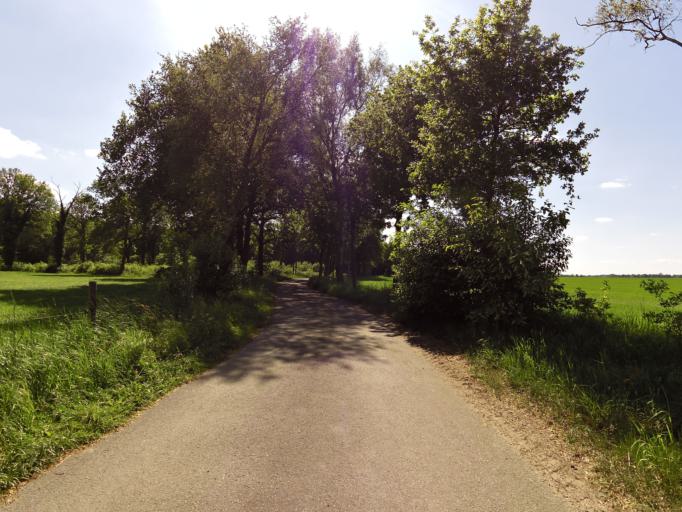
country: NL
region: Gelderland
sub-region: Gemeente Bronckhorst
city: Zelhem
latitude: 52.0518
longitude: 6.3873
